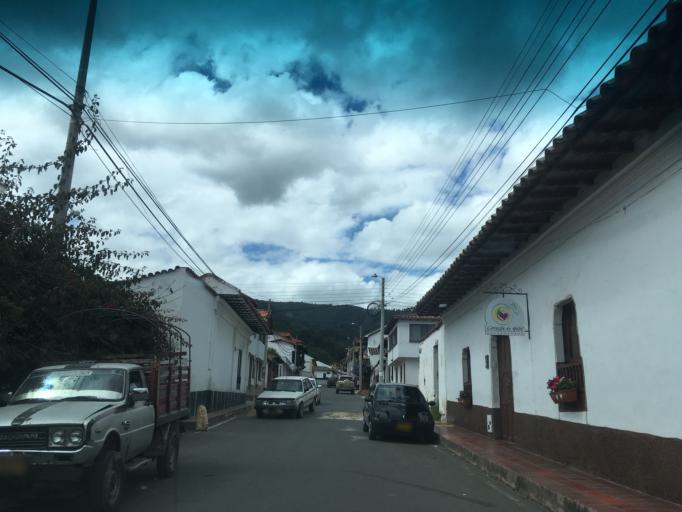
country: CO
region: Boyaca
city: Tibasosa
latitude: 5.7469
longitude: -73.0021
